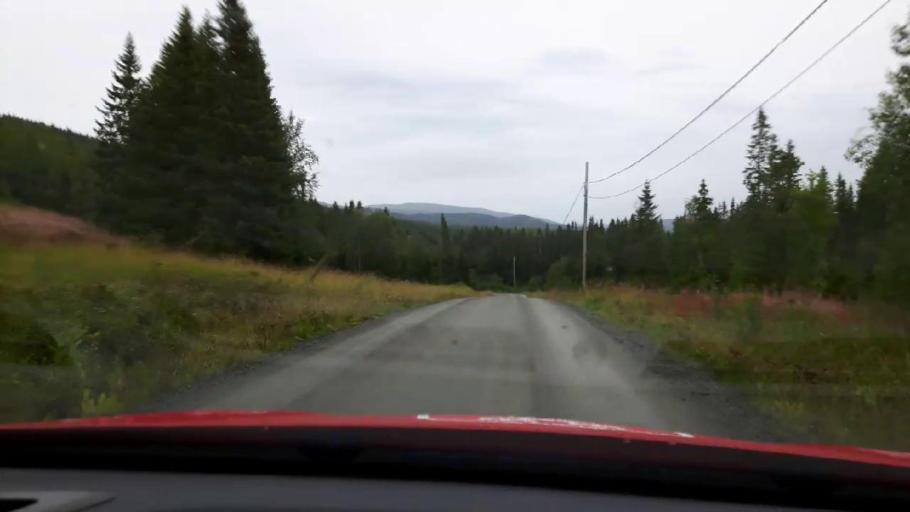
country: SE
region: Jaemtland
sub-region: Are Kommun
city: Are
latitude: 63.5021
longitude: 12.7524
